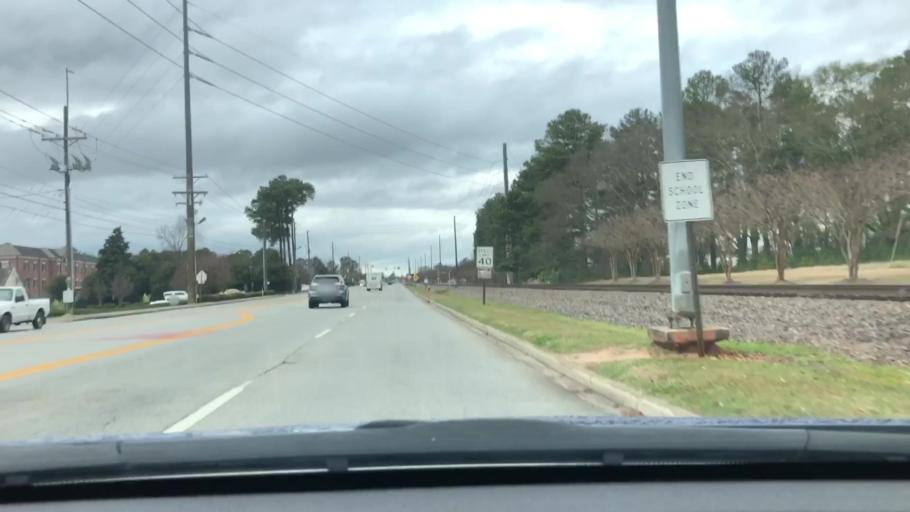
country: US
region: South Carolina
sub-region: Lexington County
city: Irmo
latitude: 34.0759
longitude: -81.1775
